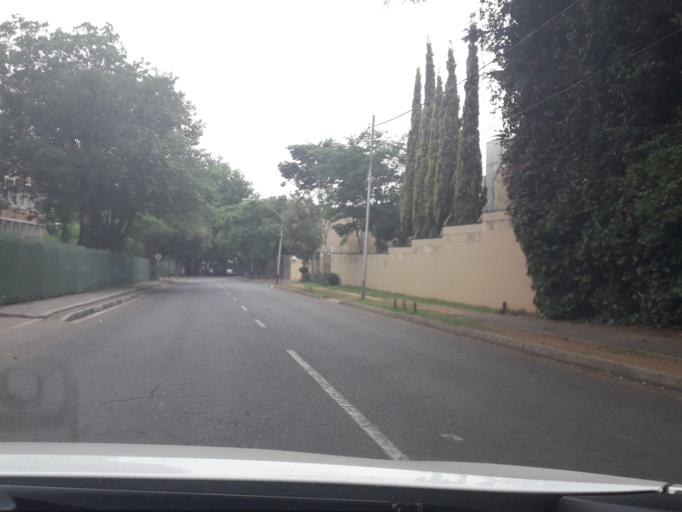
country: ZA
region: Gauteng
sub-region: City of Johannesburg Metropolitan Municipality
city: Johannesburg
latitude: -26.1341
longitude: 28.0603
